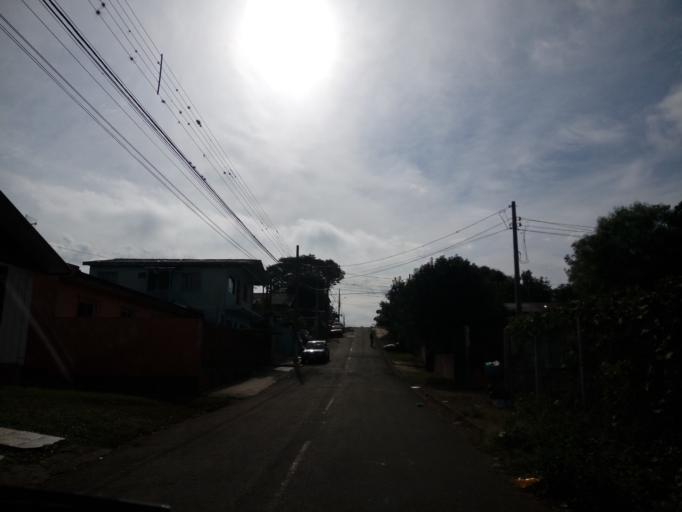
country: BR
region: Santa Catarina
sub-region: Chapeco
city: Chapeco
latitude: -27.1001
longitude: -52.6345
